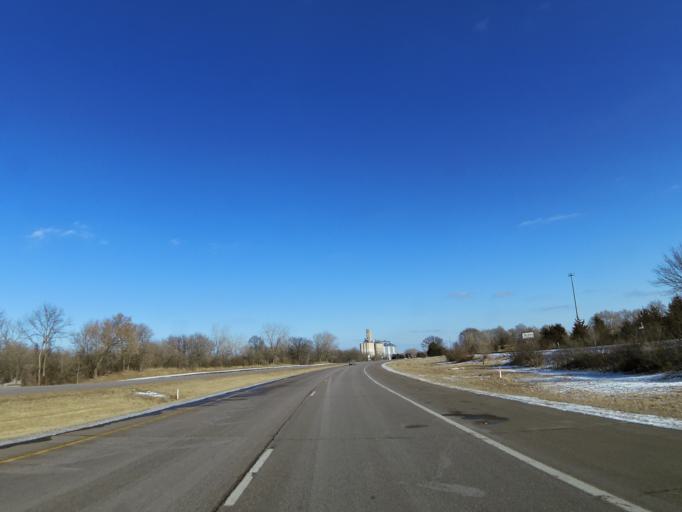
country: US
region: Minnesota
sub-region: Scott County
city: Shakopee
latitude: 44.8027
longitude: -93.4875
